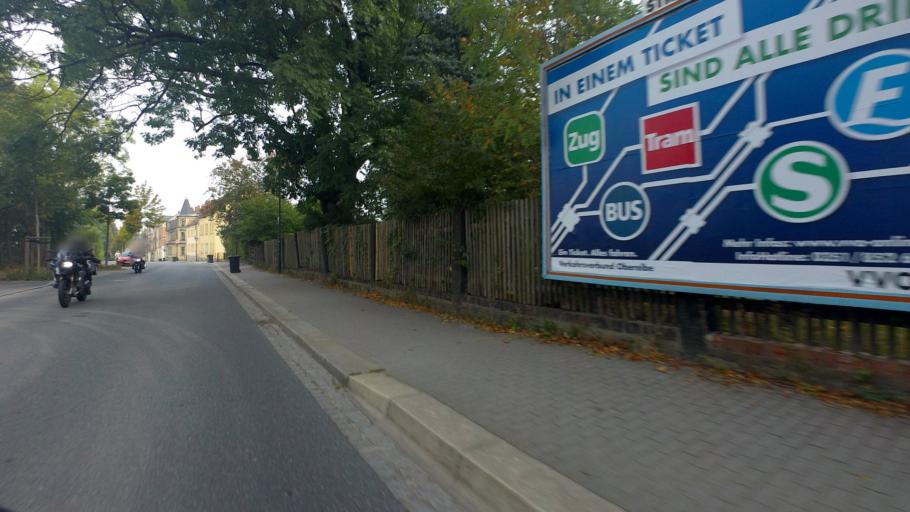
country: DE
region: Saxony
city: Radeberg
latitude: 51.1127
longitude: 13.9173
